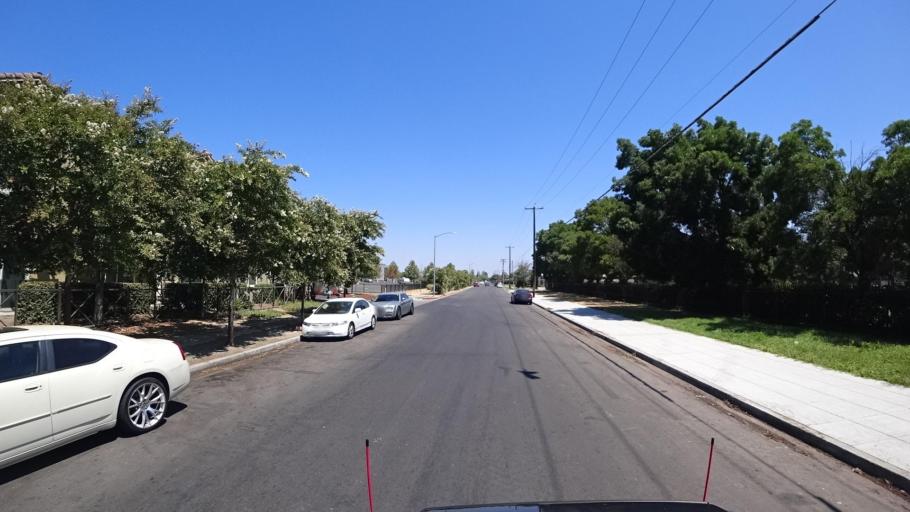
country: US
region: California
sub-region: Fresno County
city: Fresno
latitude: 36.7706
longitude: -119.7770
